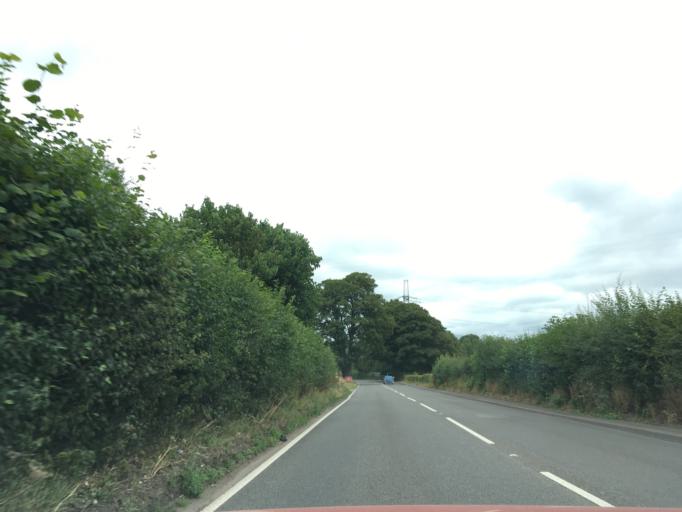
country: GB
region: Wales
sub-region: Monmouthshire
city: Abergavenny
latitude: 51.8048
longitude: -3.0078
